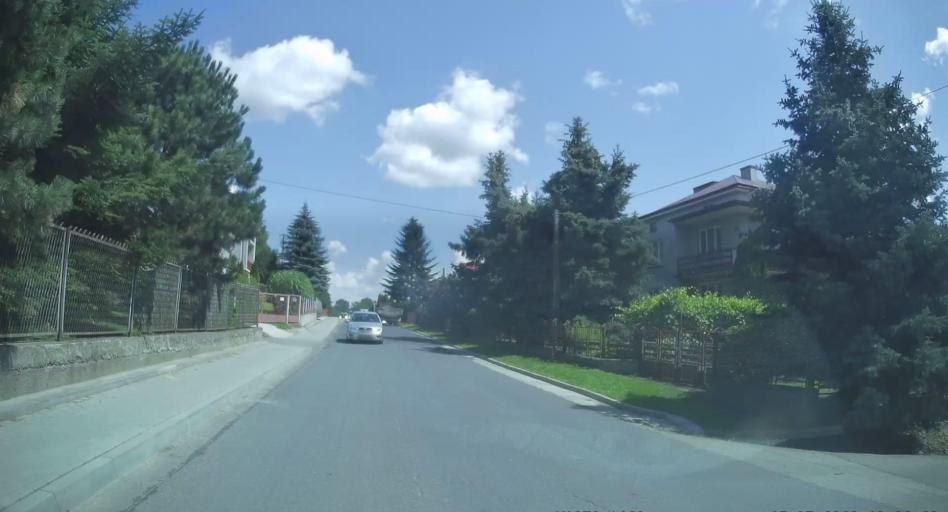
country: PL
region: Subcarpathian Voivodeship
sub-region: Powiat przemyski
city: Medyka
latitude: 49.8433
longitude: 22.8860
